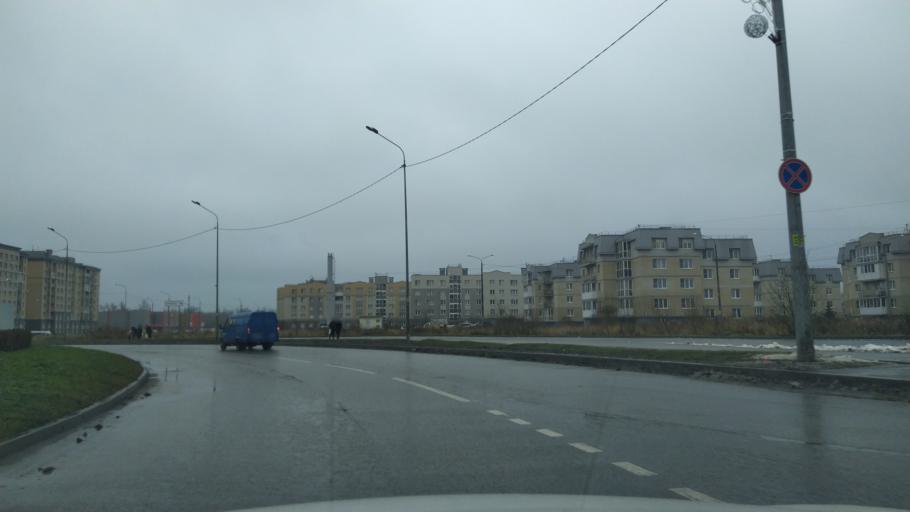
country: RU
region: St.-Petersburg
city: Tyarlevo
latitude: 59.7370
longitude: 30.4647
